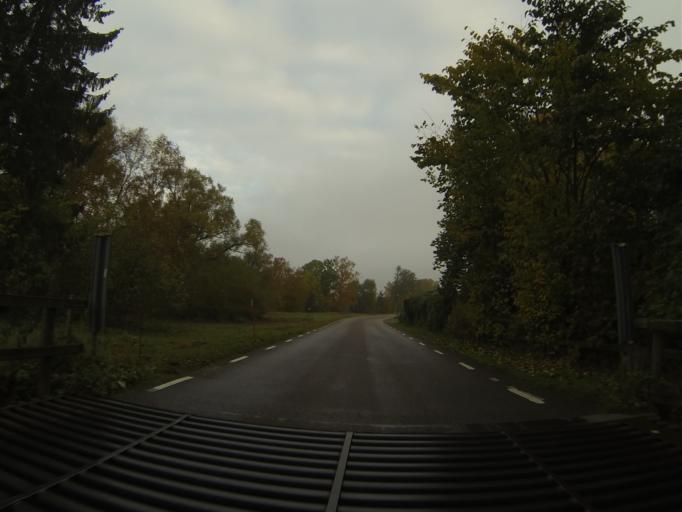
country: SE
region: Skane
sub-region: Lunds Kommun
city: Veberod
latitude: 55.6823
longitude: 13.4981
